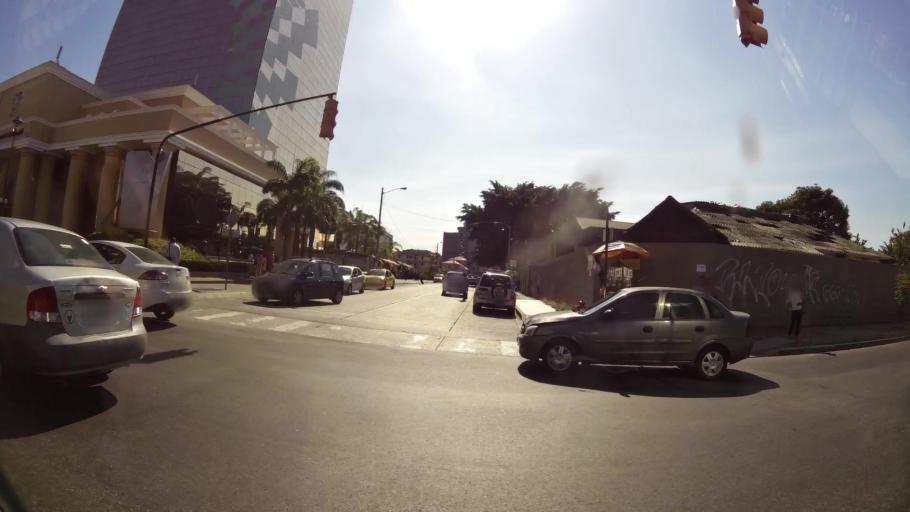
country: EC
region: Guayas
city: Guayaquil
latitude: -2.1626
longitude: -79.8978
